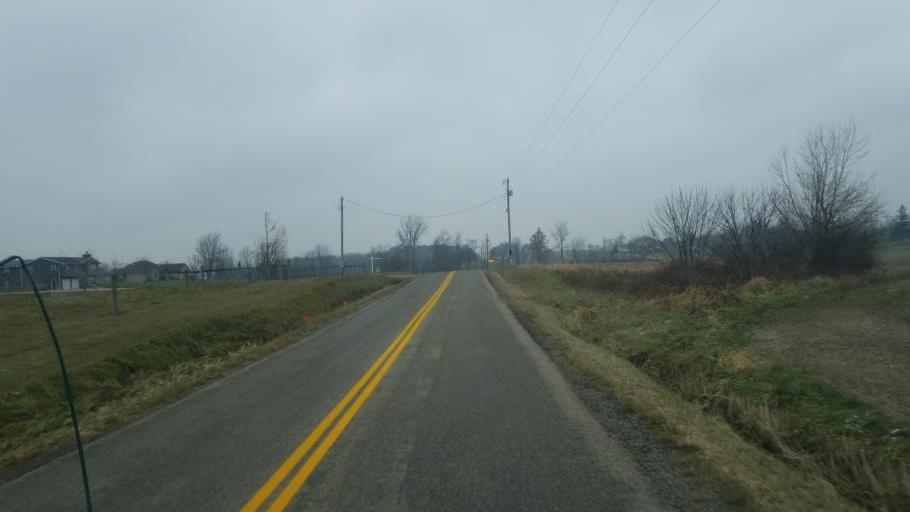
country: US
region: Ohio
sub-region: Huron County
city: New London
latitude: 41.0132
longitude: -82.3549
